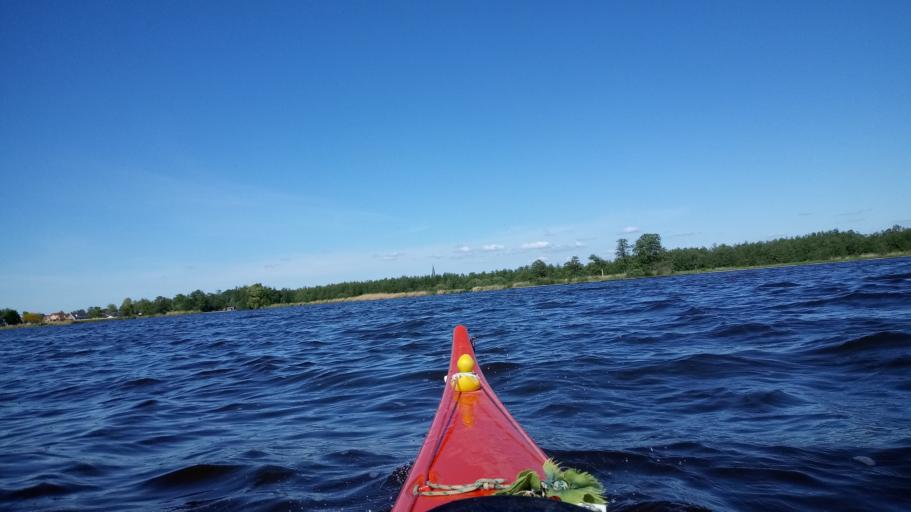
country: NL
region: South Holland
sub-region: Gemeente Nieuwkoop
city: Nieuwkoop
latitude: 52.1574
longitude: 4.8120
